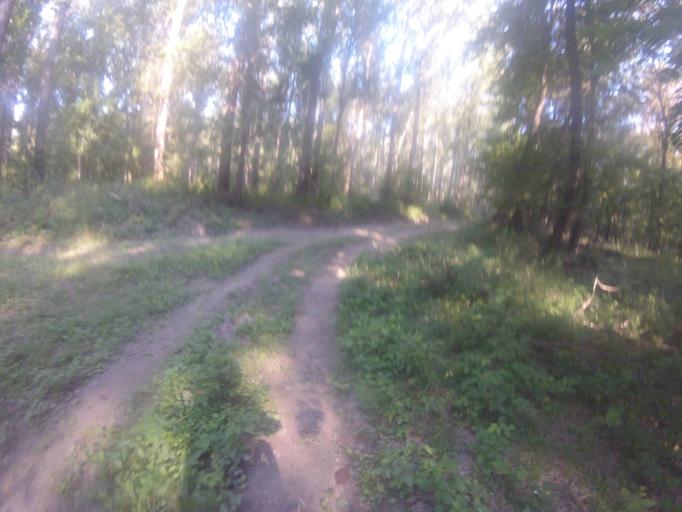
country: HU
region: Bacs-Kiskun
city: Baja
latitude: 46.1861
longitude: 18.9176
